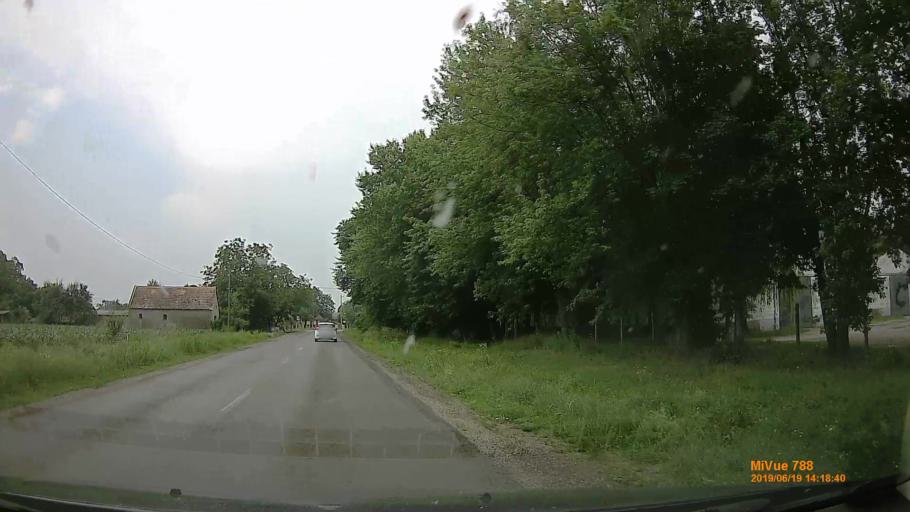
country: HU
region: Baranya
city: Szigetvar
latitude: 46.0401
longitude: 17.7822
